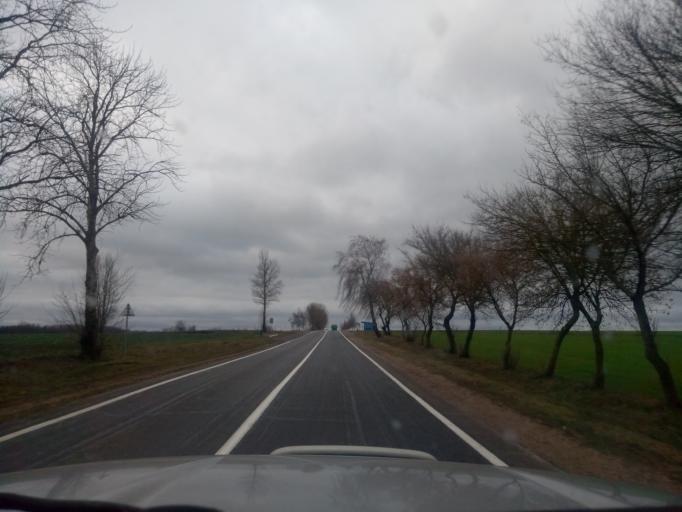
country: BY
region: Minsk
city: Kapyl'
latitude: 53.1835
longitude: 27.1777
